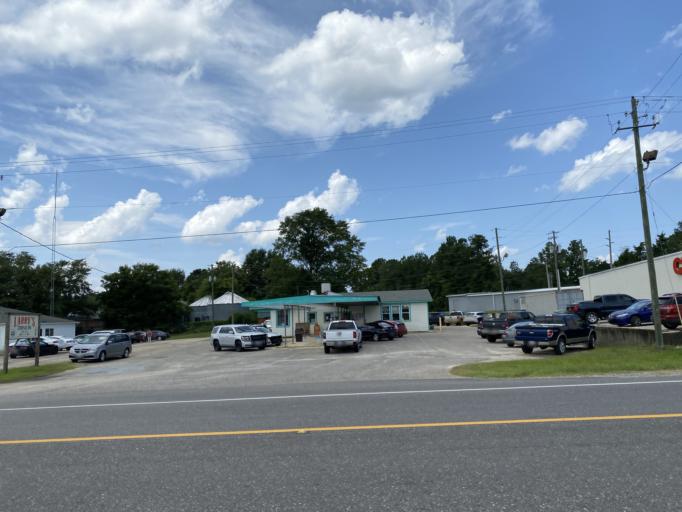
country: US
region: Alabama
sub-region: Wilcox County
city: Camden
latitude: 31.9955
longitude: -87.2786
